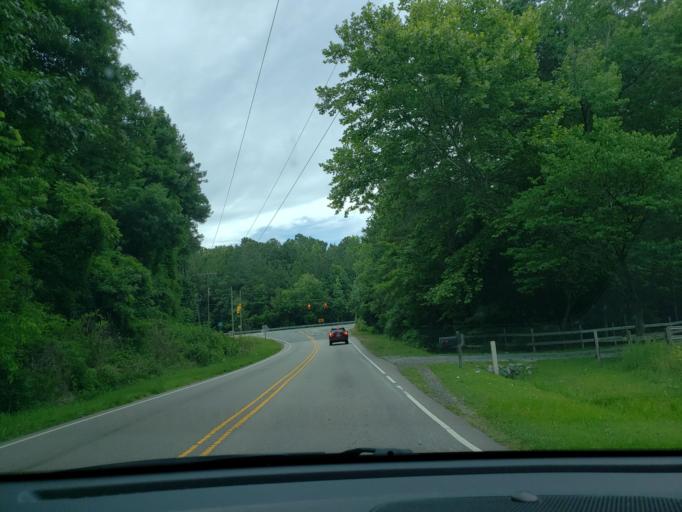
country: US
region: North Carolina
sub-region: Orange County
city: Chapel Hill
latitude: 35.8864
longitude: -78.9891
